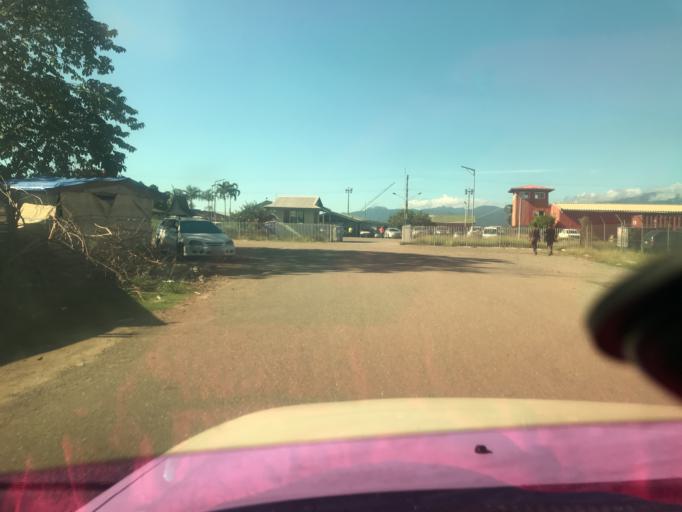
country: SB
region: Guadalcanal
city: Honiara
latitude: -9.4278
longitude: 160.0478
